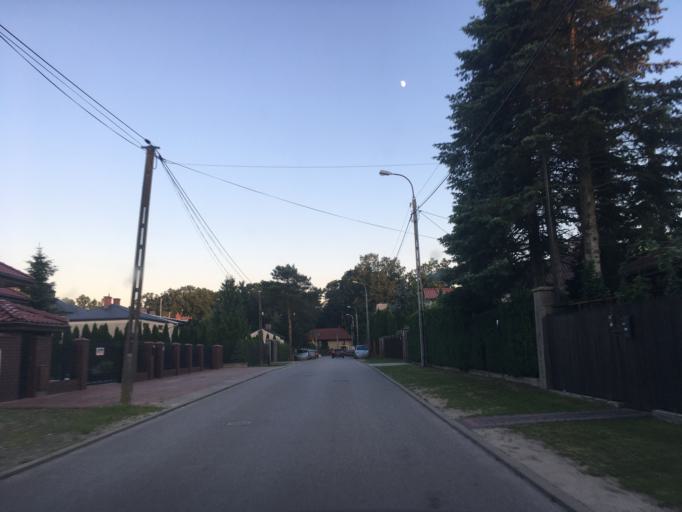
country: PL
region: Masovian Voivodeship
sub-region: Powiat piaseczynski
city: Piaseczno
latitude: 52.0653
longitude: 21.0118
